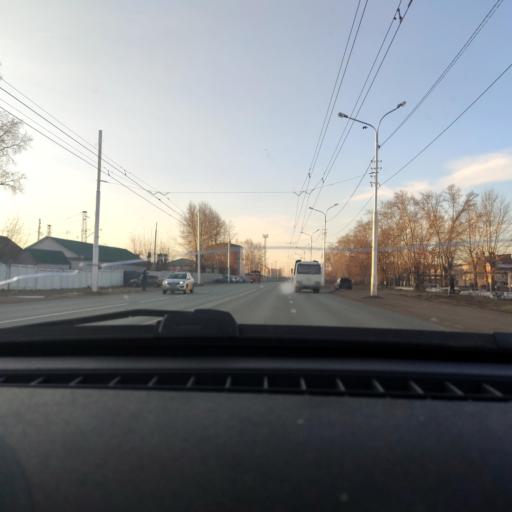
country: RU
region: Bashkortostan
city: Ufa
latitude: 54.8334
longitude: 56.0894
